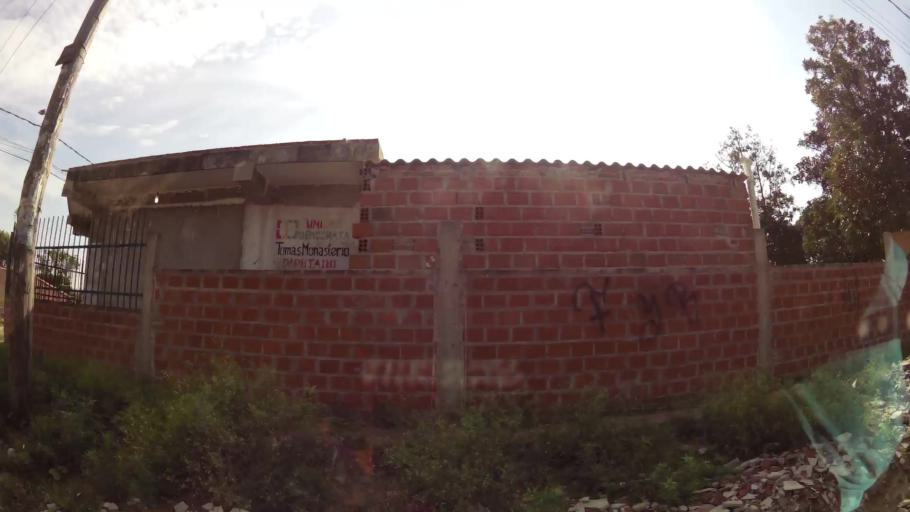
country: BO
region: Santa Cruz
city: Santa Cruz de la Sierra
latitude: -17.7339
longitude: -63.1342
